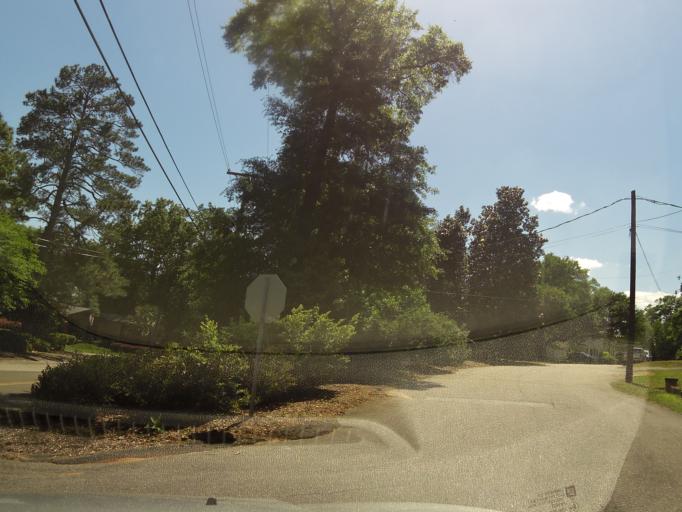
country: US
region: South Carolina
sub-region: Aiken County
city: Aiken
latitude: 33.5591
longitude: -81.7262
